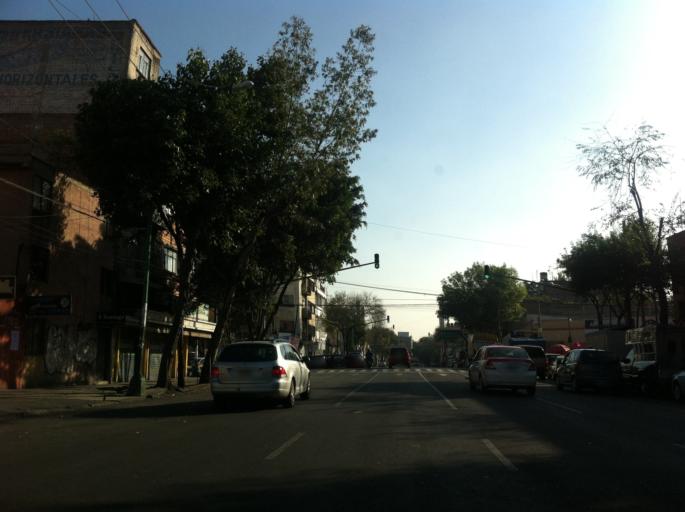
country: MX
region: Mexico City
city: Benito Juarez
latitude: 19.4189
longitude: -99.1504
